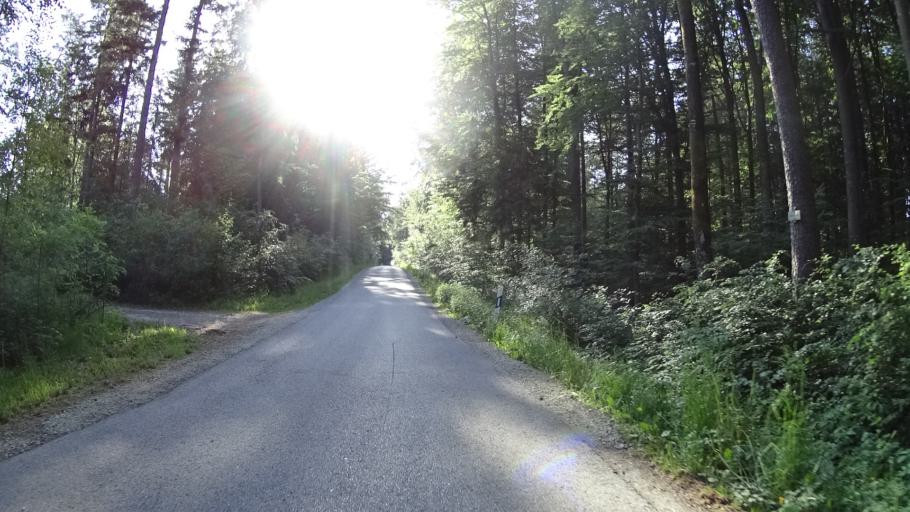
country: DE
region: Bavaria
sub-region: Regierungsbezirk Mittelfranken
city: Lichtenau
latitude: 49.1503
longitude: 10.3942
